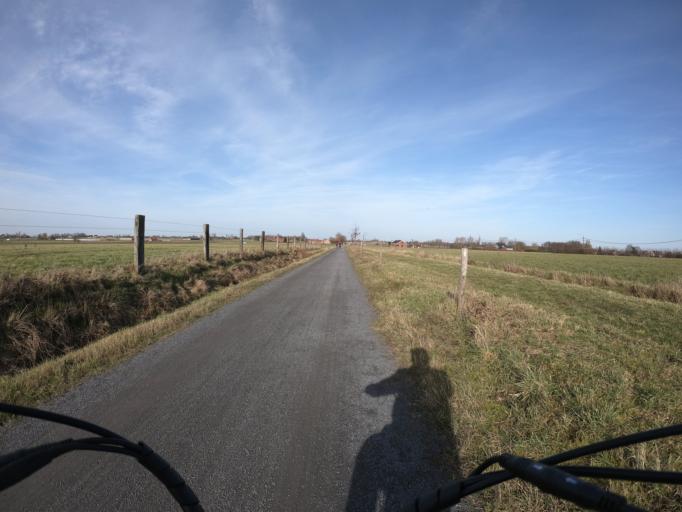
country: BE
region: Flanders
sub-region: Provincie West-Vlaanderen
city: Ledegem
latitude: 50.8675
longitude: 3.1252
